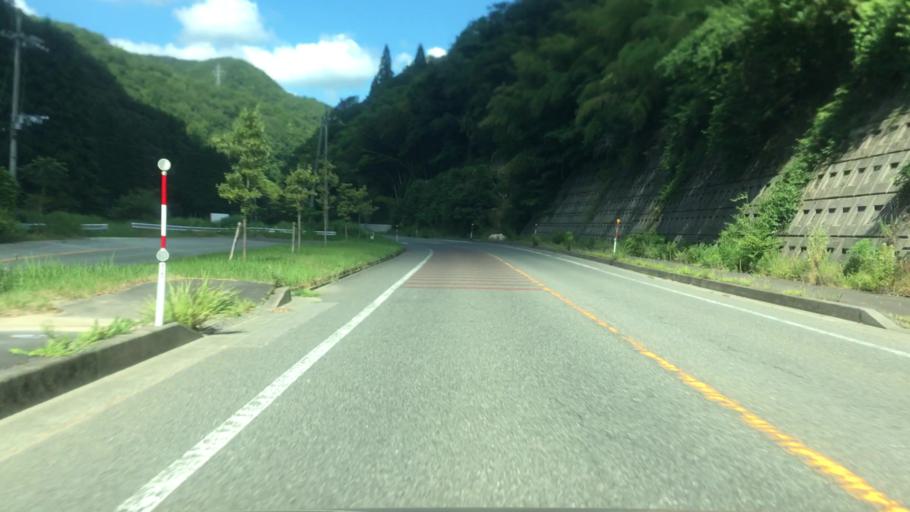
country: JP
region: Hyogo
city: Toyooka
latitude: 35.5761
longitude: 134.7611
